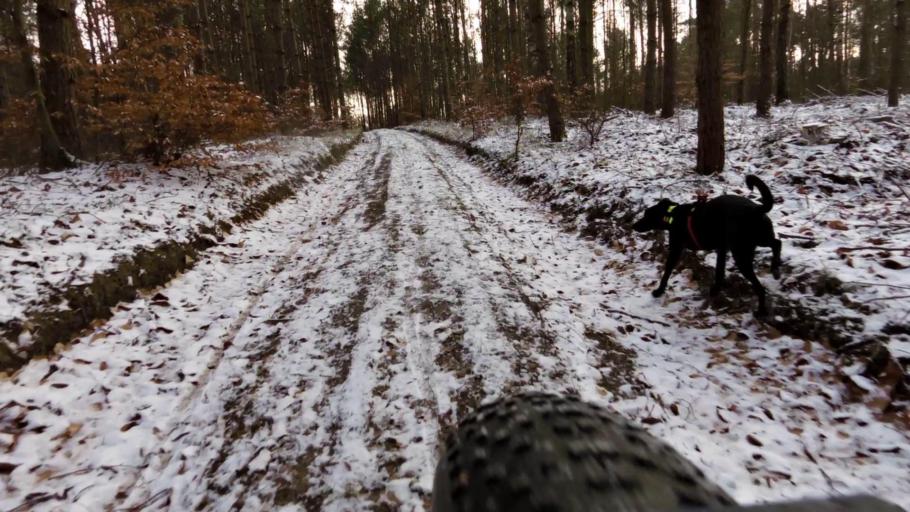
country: PL
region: West Pomeranian Voivodeship
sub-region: Powiat walecki
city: Walcz
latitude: 53.2890
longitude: 16.2986
